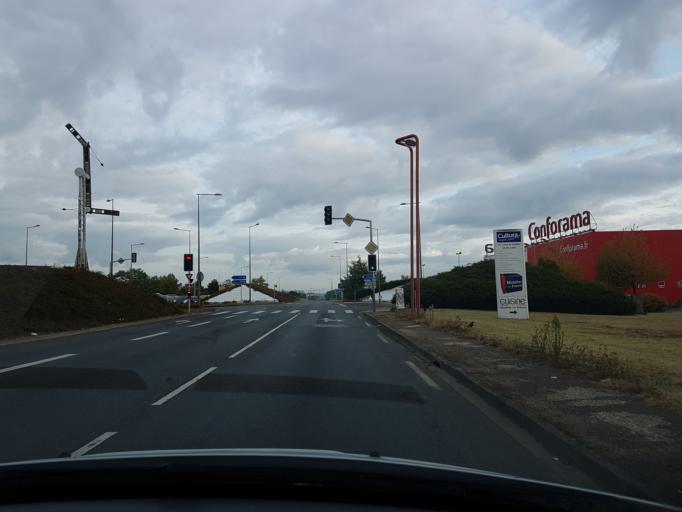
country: FR
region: Centre
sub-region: Departement d'Indre-et-Loire
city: Chambray-les-Tours
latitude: 47.3439
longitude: 0.7026
